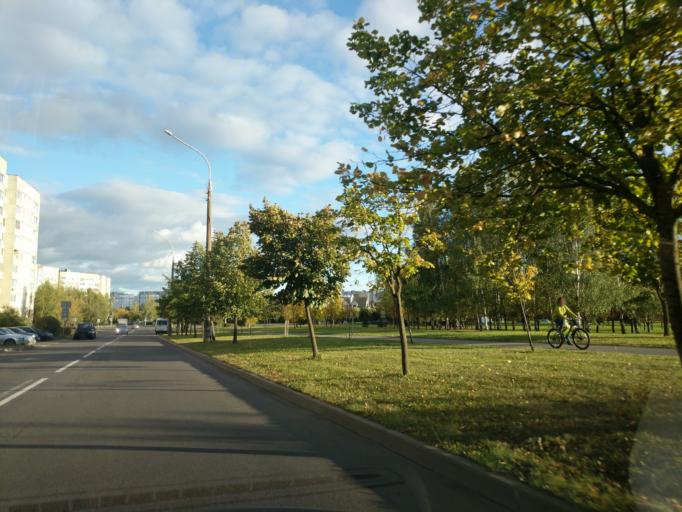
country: BY
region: Minsk
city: Malinovka
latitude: 53.8585
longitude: 27.4538
